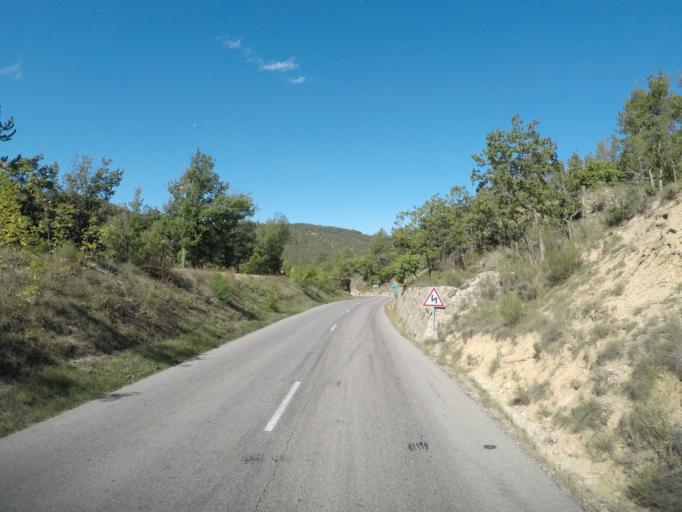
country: FR
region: Provence-Alpes-Cote d'Azur
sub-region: Departement des Alpes-de-Haute-Provence
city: Mallemoisson
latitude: 44.0242
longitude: 6.1740
